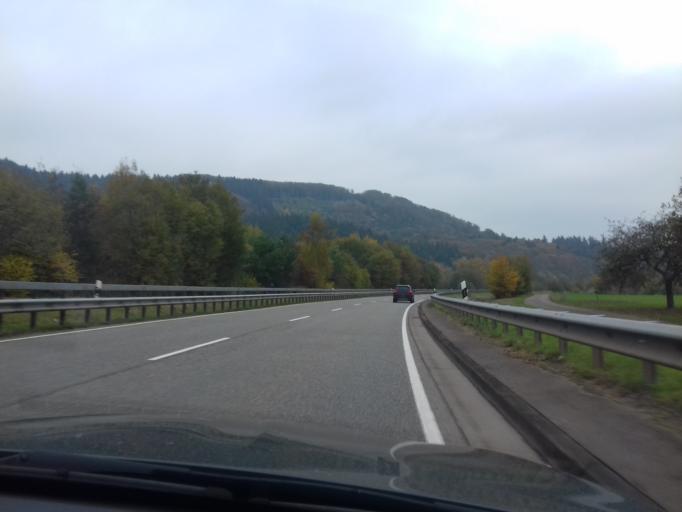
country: DE
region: Rheinland-Pfalz
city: Wawern
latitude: 49.6461
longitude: 6.5330
